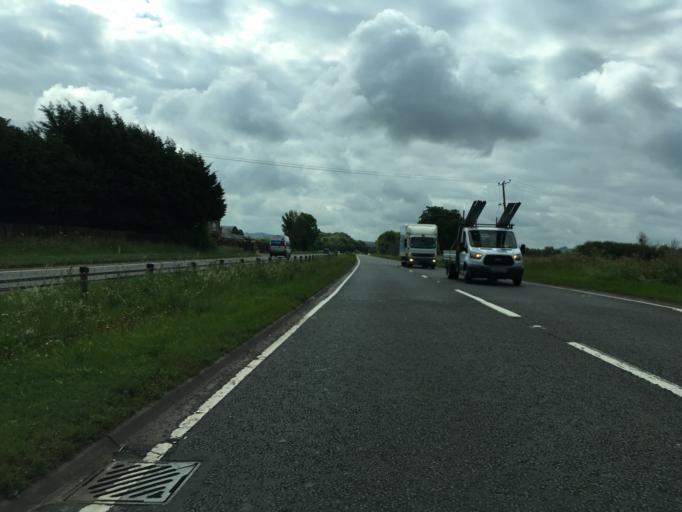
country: GB
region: England
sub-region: Borough of Swindon
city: Wanborough
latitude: 51.5699
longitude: -1.7275
